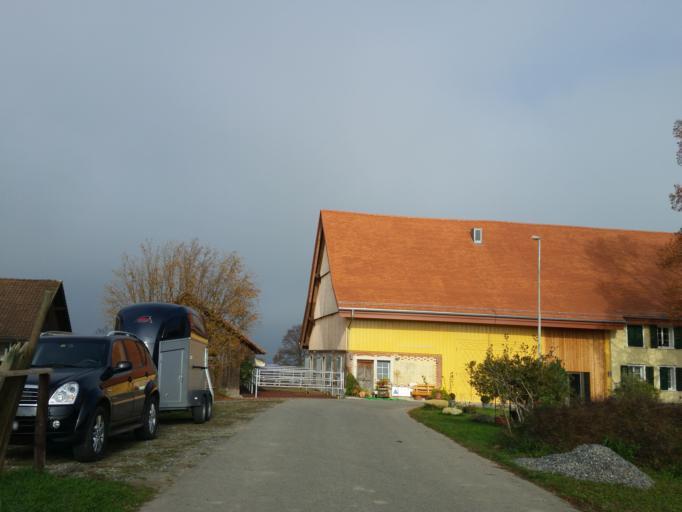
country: CH
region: Thurgau
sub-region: Arbon District
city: Egnach
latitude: 47.5311
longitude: 9.4056
